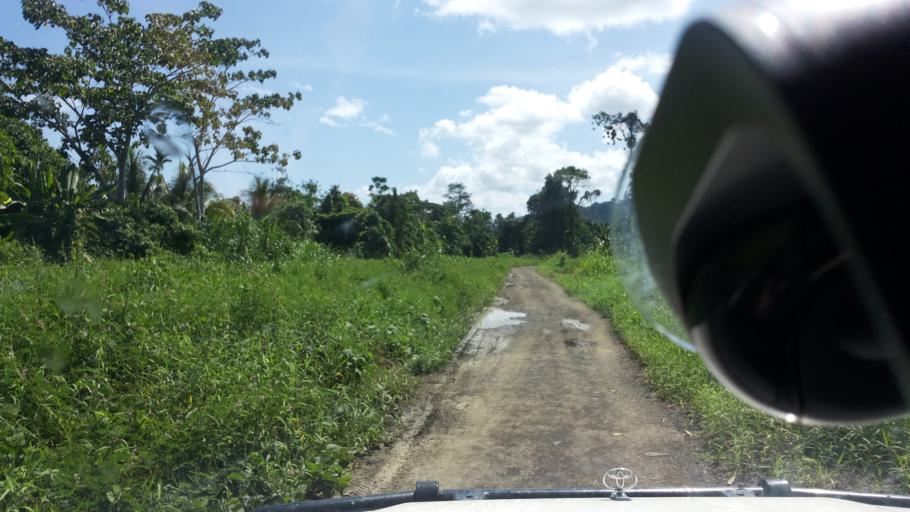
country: PG
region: Madang
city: Madang
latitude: -5.5168
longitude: 145.3549
